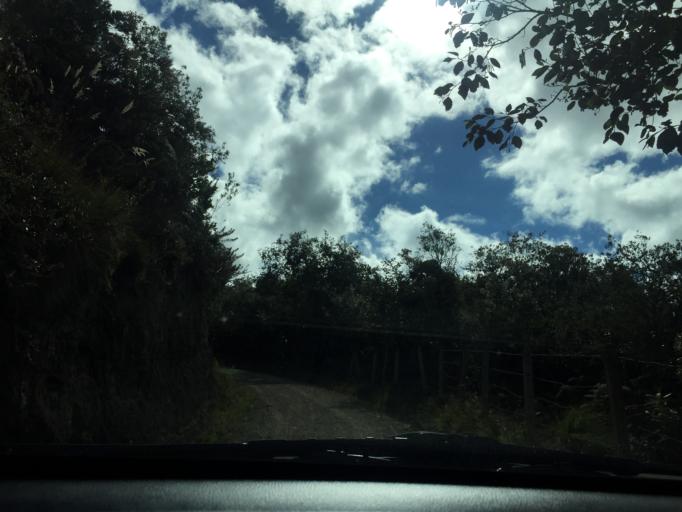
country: CO
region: Cundinamarca
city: Tocancipa
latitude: 4.9582
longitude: -73.8815
